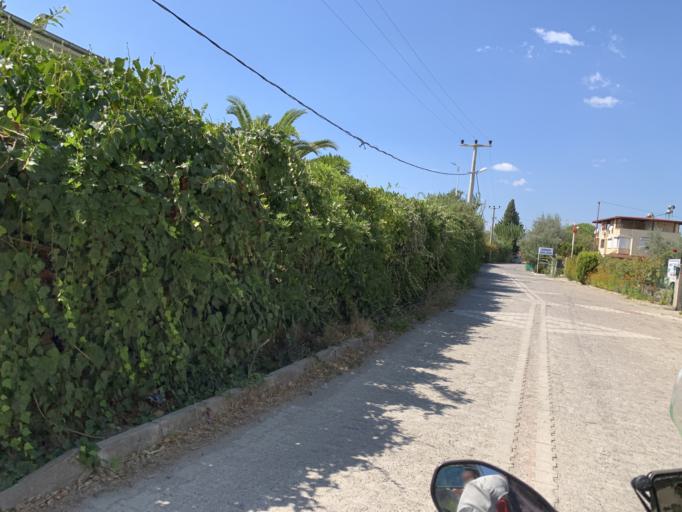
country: TR
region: Balikesir
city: Altinoluk
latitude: 39.5629
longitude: 26.8347
